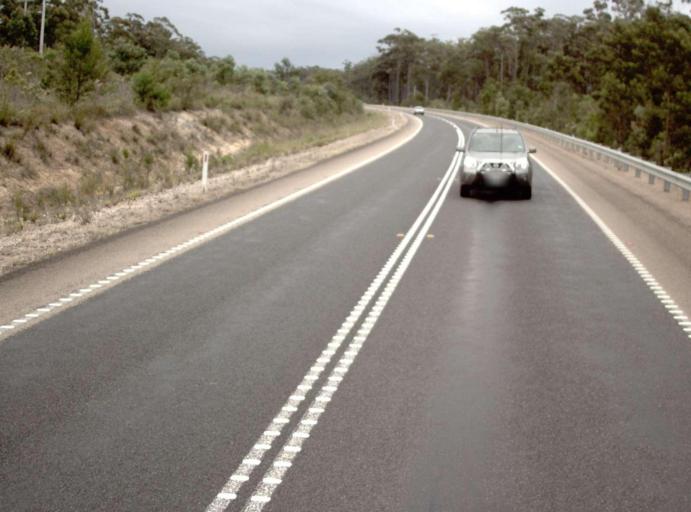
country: AU
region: Victoria
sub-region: East Gippsland
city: Lakes Entrance
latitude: -37.6985
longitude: 148.0492
